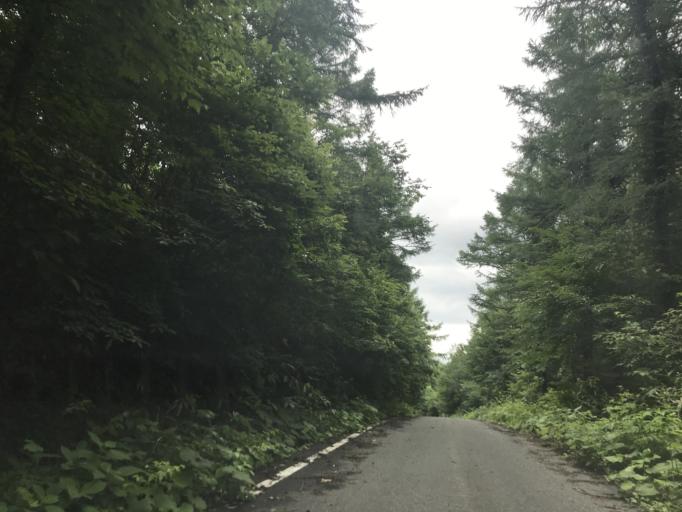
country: JP
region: Iwate
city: Ichinoseki
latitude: 38.9386
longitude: 140.8768
